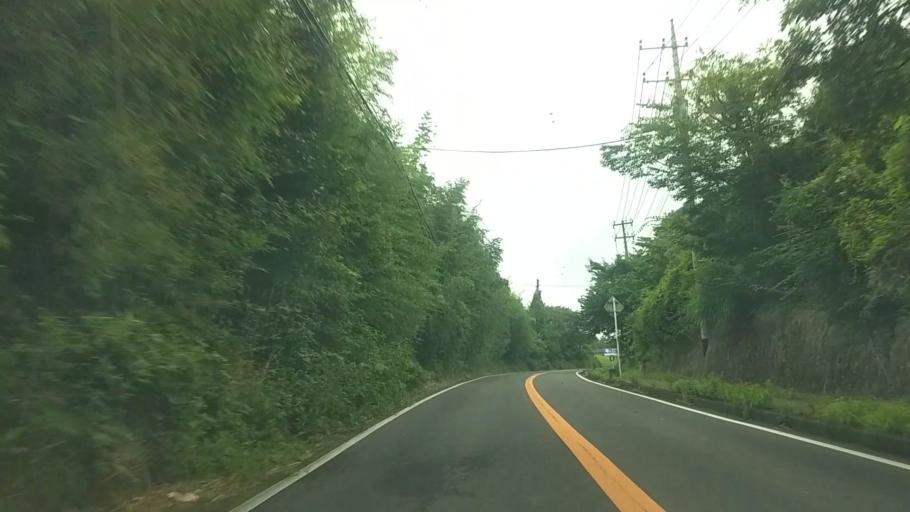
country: JP
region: Chiba
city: Kisarazu
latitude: 35.2792
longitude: 140.0767
